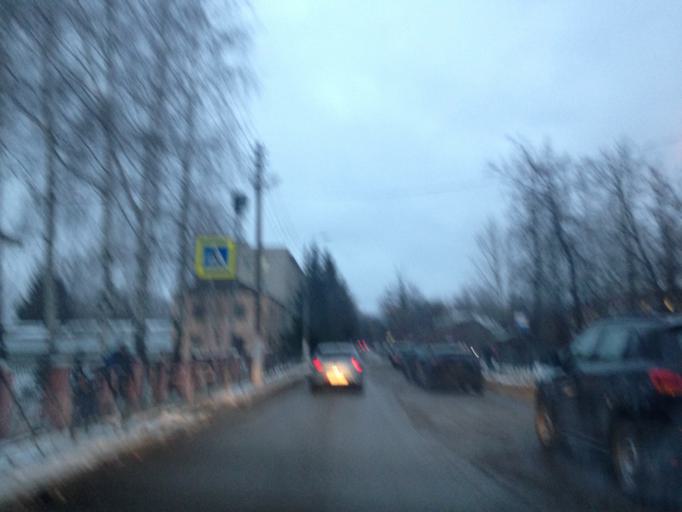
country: RU
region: Tula
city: Shchekino
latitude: 53.9981
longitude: 37.5126
